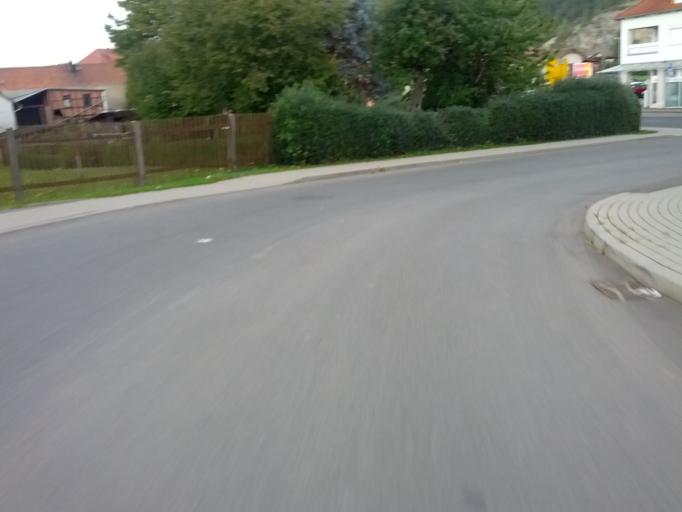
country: DE
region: Thuringia
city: Thal
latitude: 50.9554
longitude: 10.3968
